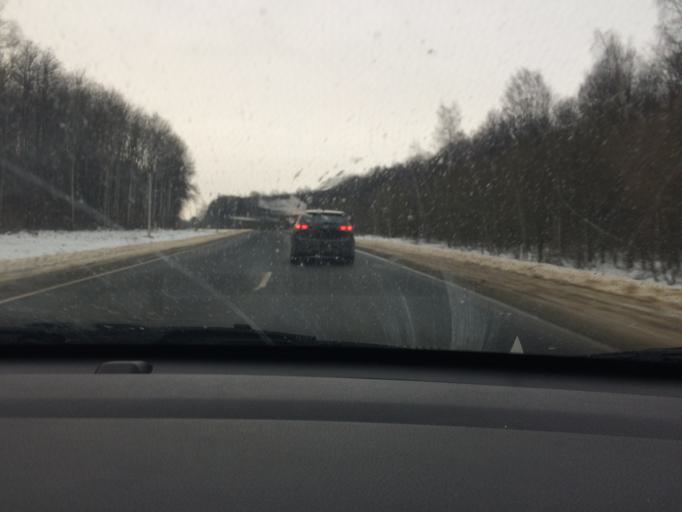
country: RU
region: Tula
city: Venev
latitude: 54.3359
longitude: 38.1293
